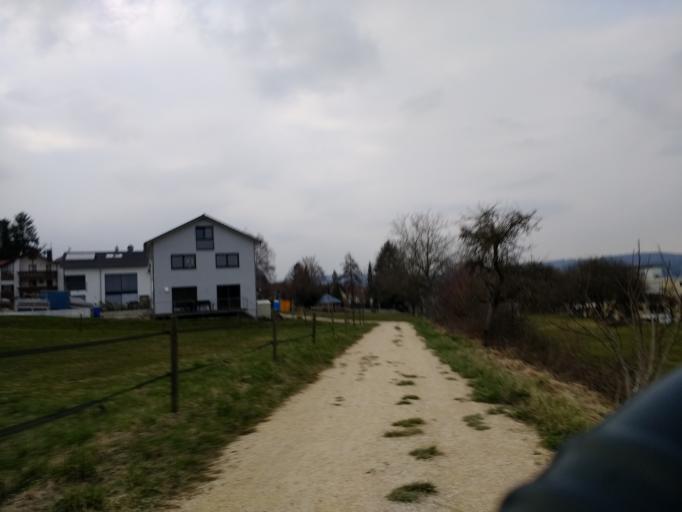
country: DE
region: Baden-Wuerttemberg
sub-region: Tuebingen Region
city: Uberlingen
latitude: 47.7449
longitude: 9.1334
